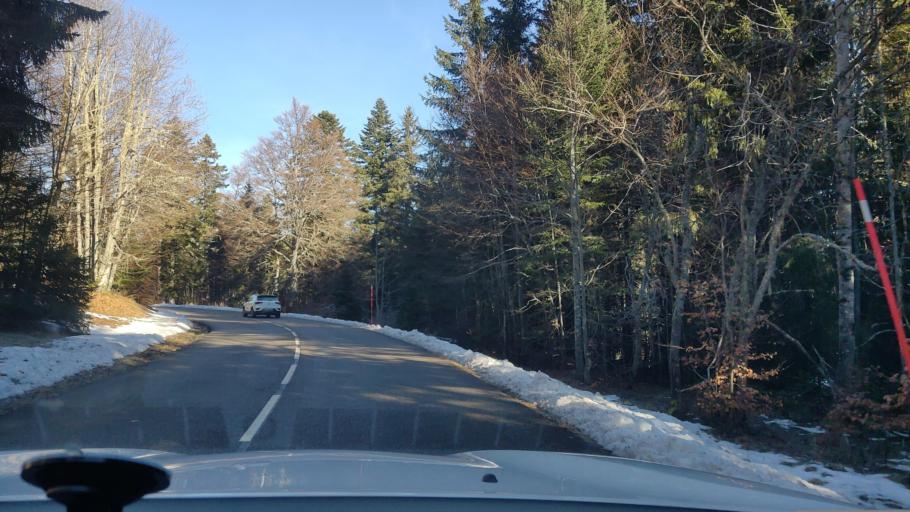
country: FR
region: Rhone-Alpes
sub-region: Departement de la Savoie
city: Mery
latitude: 45.6530
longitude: 5.9814
